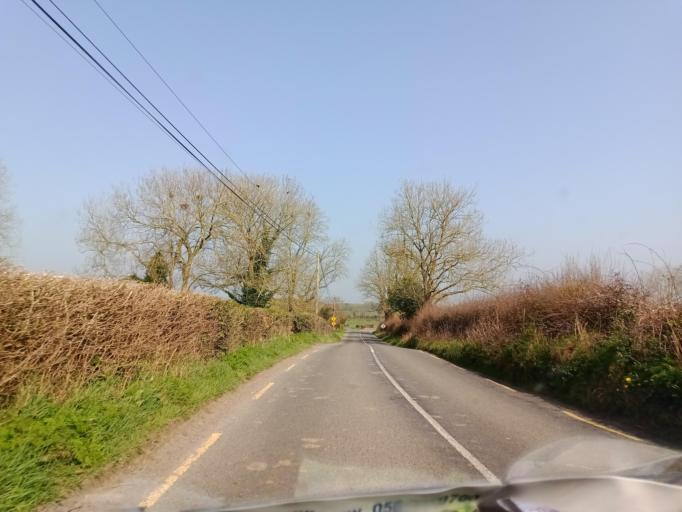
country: IE
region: Leinster
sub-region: Kilkenny
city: Callan
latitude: 52.5133
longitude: -7.3855
